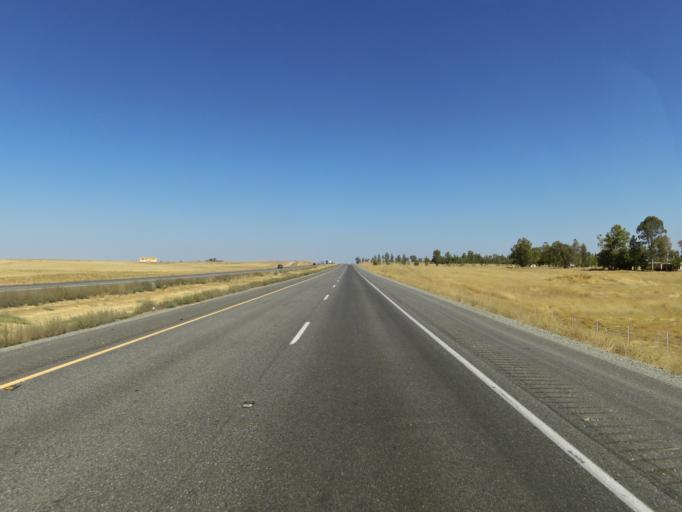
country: US
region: California
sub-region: Tehama County
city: Corning
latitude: 39.8578
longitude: -122.1999
